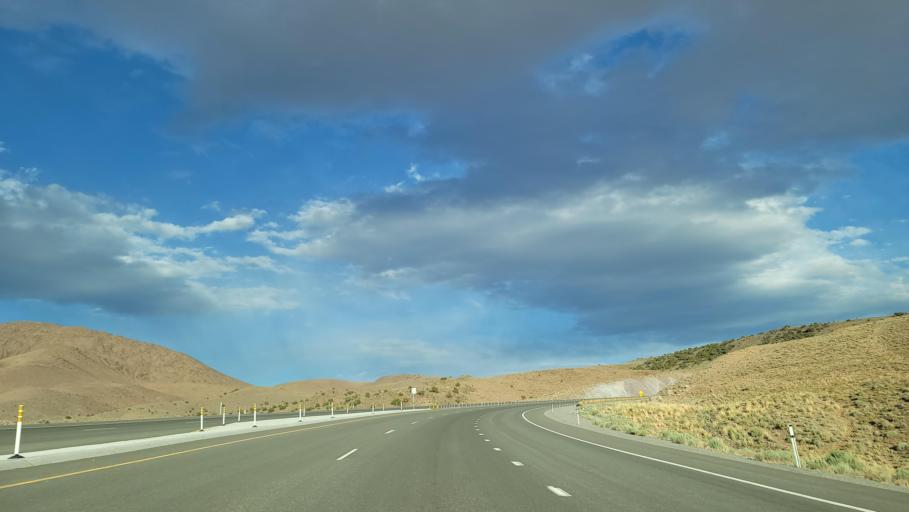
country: US
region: Nevada
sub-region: Lyon County
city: Stagecoach
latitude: 39.4906
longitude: -119.4047
